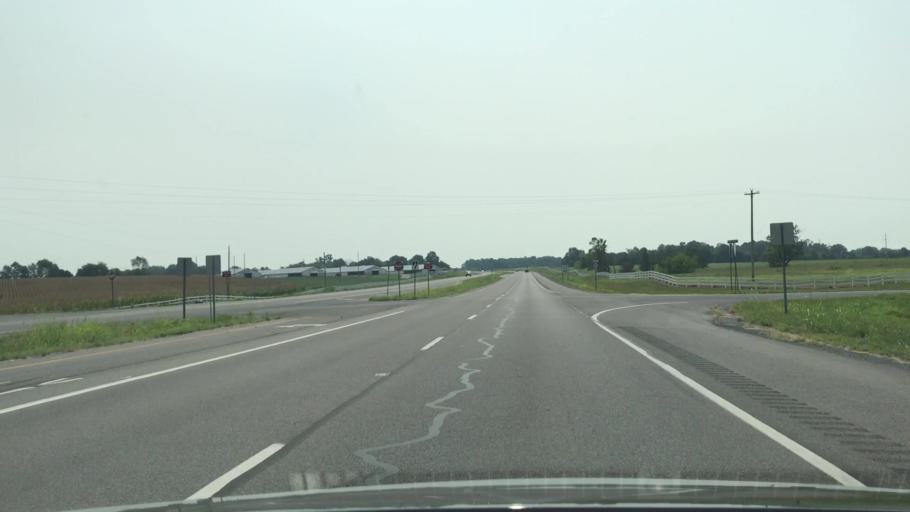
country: US
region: Kentucky
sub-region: Graves County
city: Mayfield
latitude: 36.6818
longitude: -88.5337
